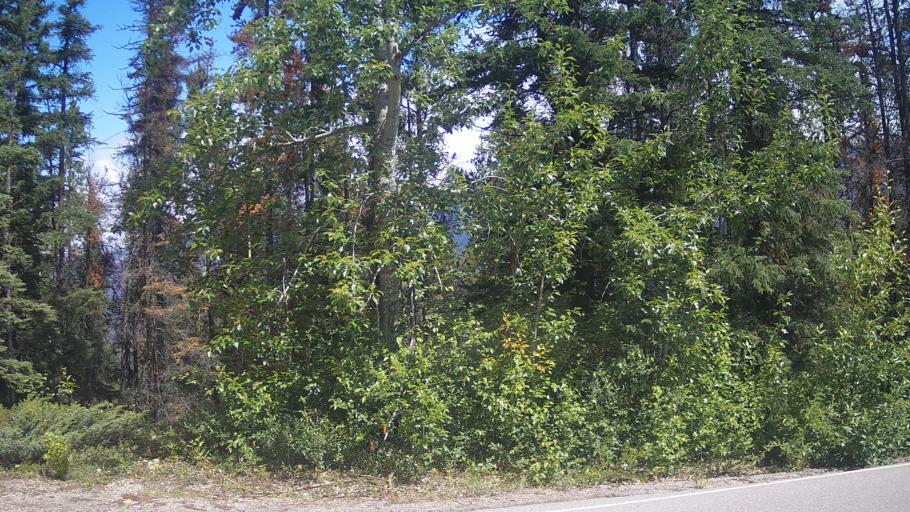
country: CA
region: Alberta
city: Jasper Park Lodge
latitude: 52.7710
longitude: -118.0331
